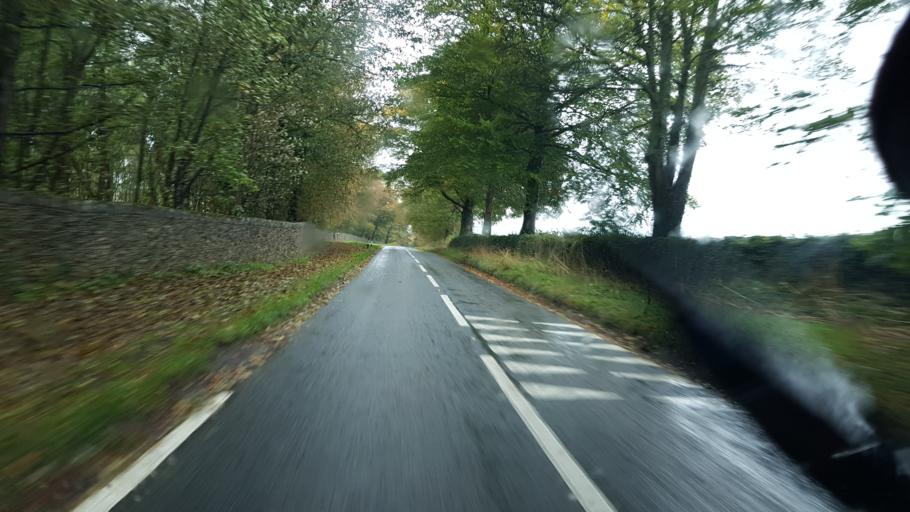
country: GB
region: England
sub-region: Gloucestershire
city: Stow on the Wold
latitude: 51.9343
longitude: -1.7288
